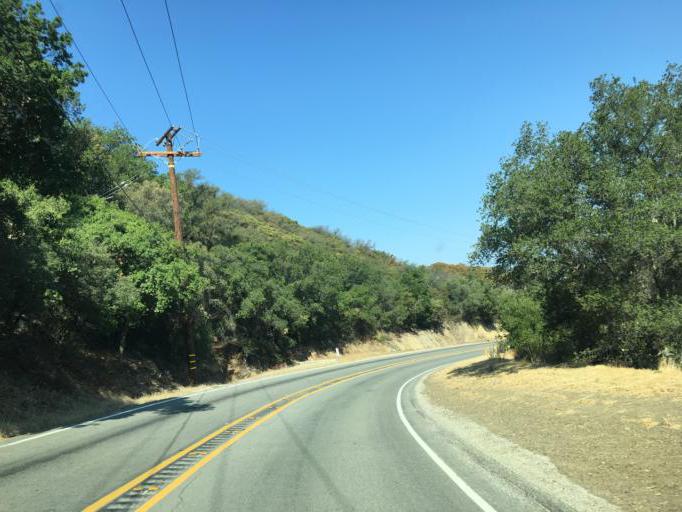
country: US
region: California
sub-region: Los Angeles County
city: Las Flores
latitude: 34.0837
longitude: -118.6512
